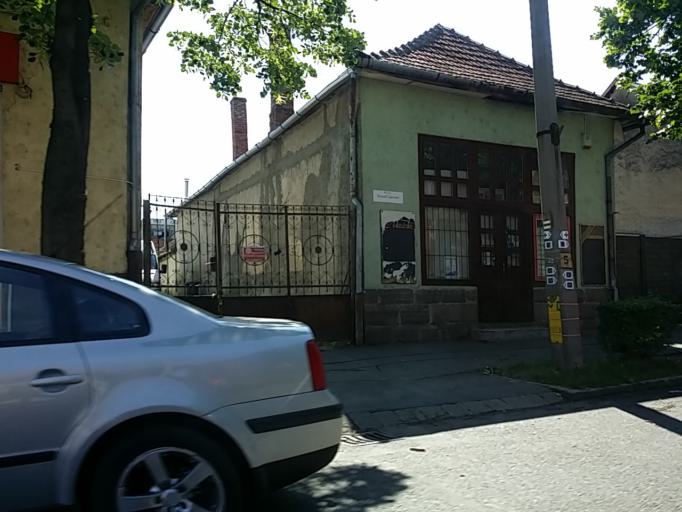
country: HU
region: Borsod-Abauj-Zemplen
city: Satoraljaujhely
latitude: 48.3922
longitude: 21.6562
